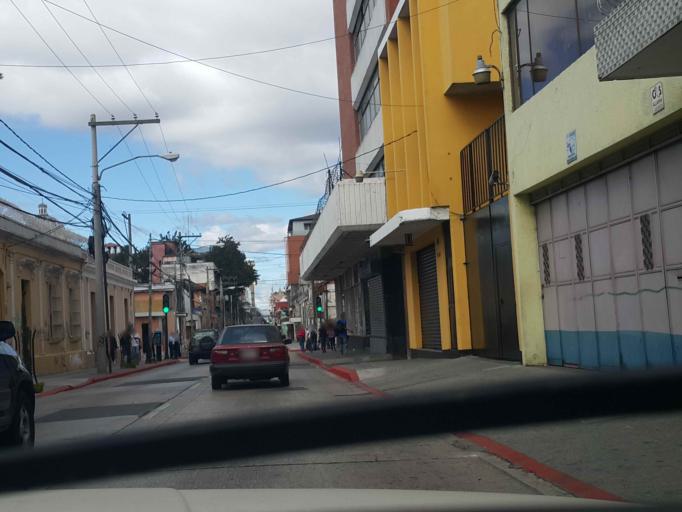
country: GT
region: Guatemala
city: Guatemala City
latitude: 14.6328
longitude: -90.5136
